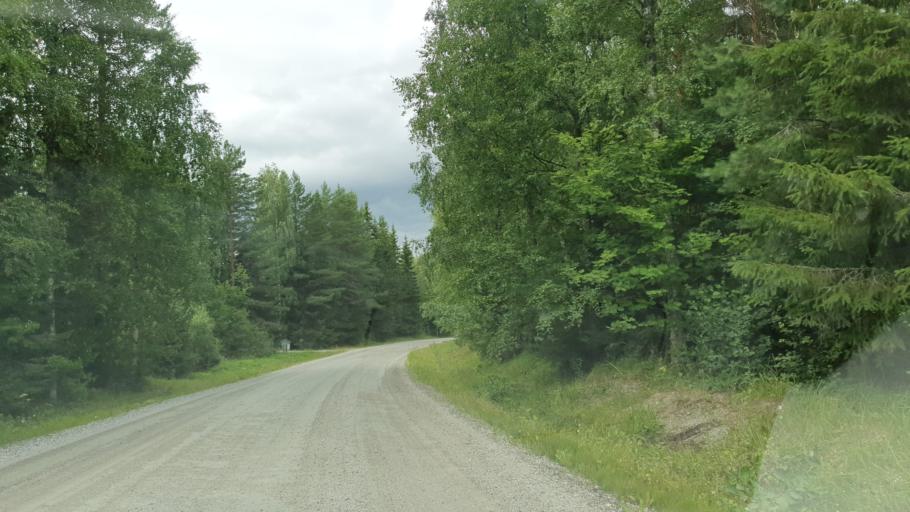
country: FI
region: Northern Savo
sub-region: Ylae-Savo
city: Iisalmi
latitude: 63.5377
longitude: 27.0755
